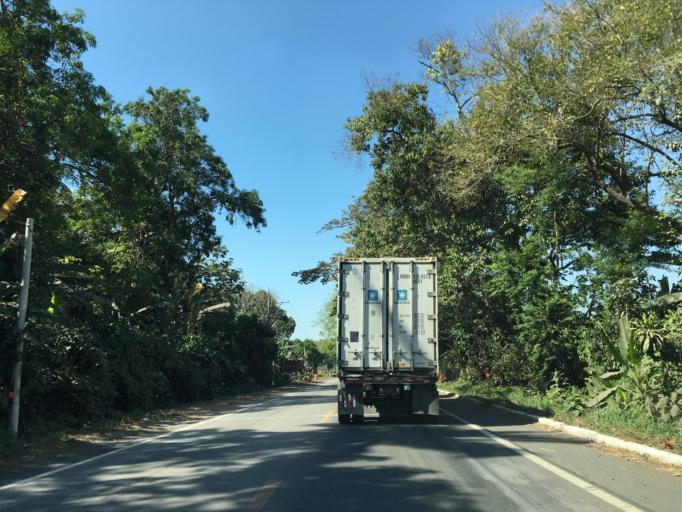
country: GT
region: Escuintla
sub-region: Municipio de Masagua
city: Masagua
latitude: 14.1830
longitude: -90.8639
